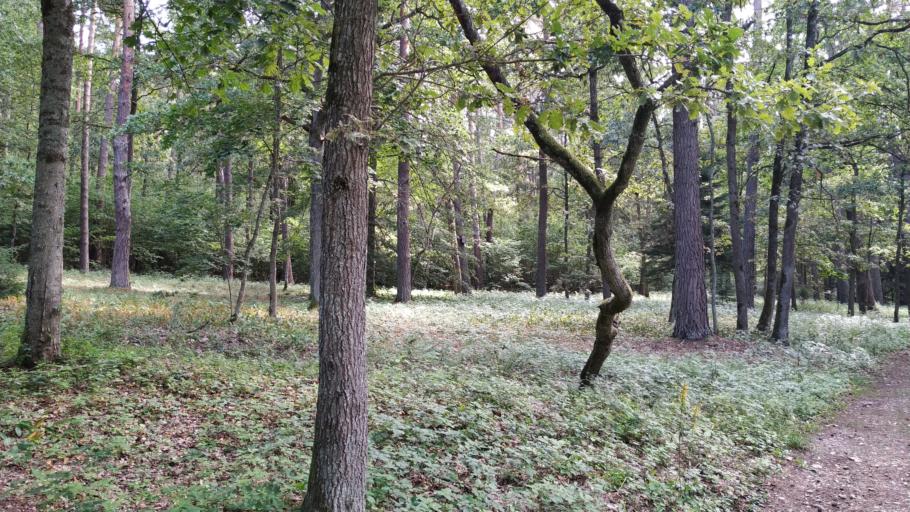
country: LT
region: Vilnius County
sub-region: Vilniaus Rajonas
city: Vievis
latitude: 54.8139
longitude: 24.9626
